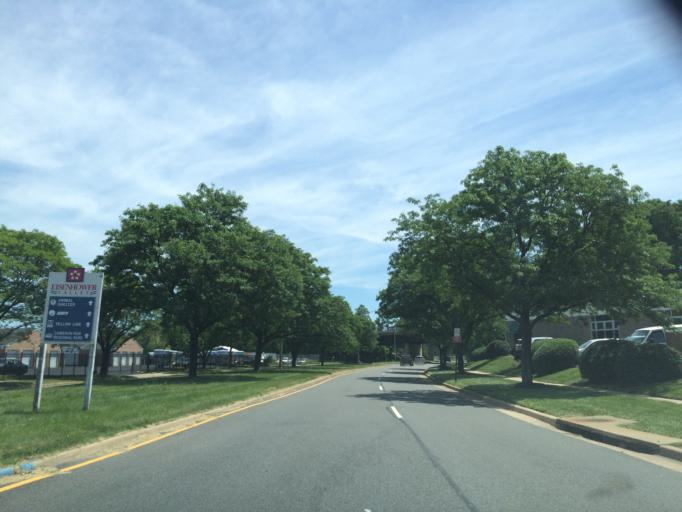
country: US
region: Virginia
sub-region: Fairfax County
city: Rose Hill
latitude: 38.8044
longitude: -77.1118
